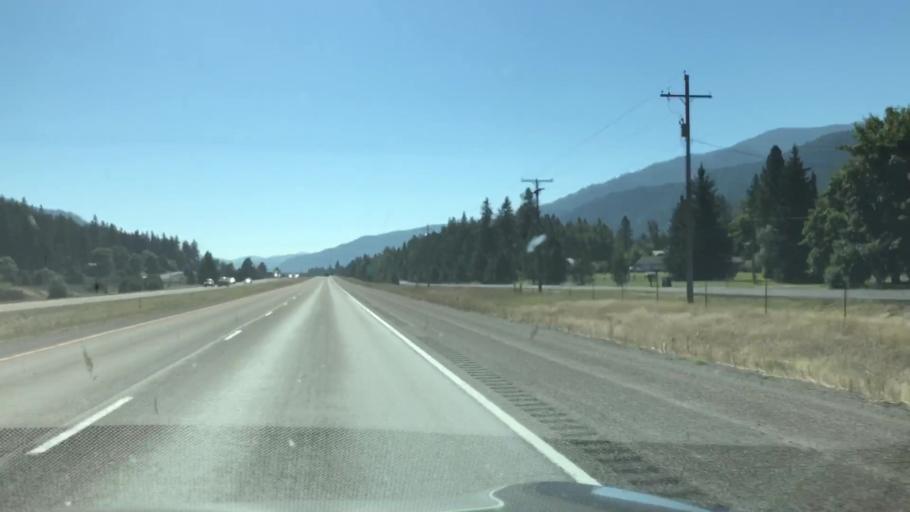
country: US
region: Montana
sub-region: Missoula County
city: Bonner-West Riverside
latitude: 46.8494
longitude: -113.8515
